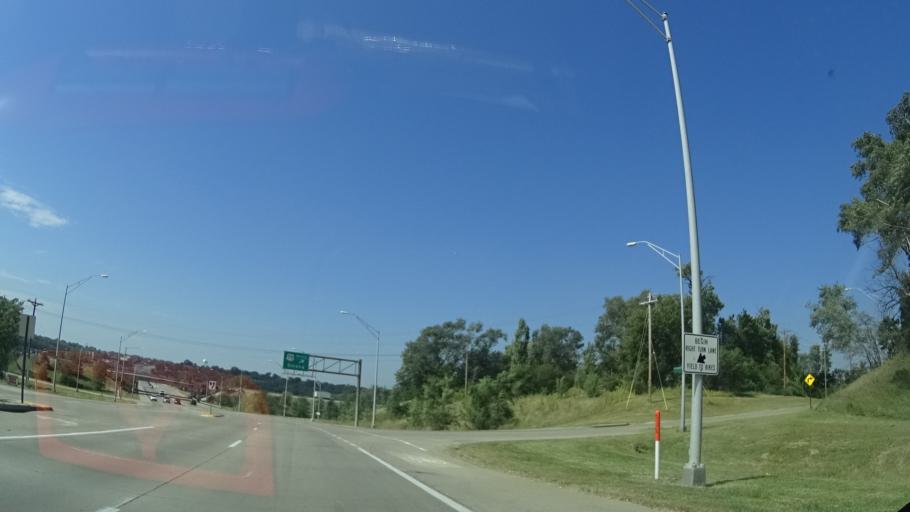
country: US
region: Nebraska
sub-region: Sarpy County
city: Offutt Air Force Base
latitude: 41.1175
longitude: -95.9317
